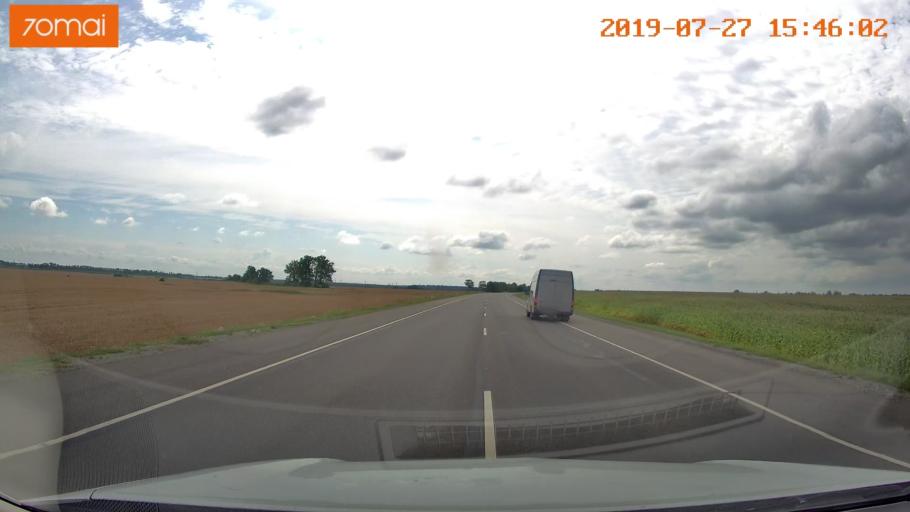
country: RU
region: Kaliningrad
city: Gusev
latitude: 54.6066
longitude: 22.1244
